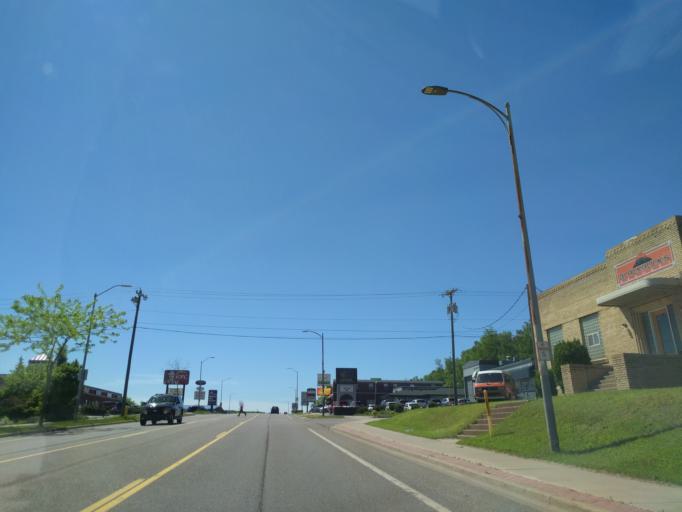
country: US
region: Michigan
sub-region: Marquette County
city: Marquette
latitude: 46.5459
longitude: -87.4145
